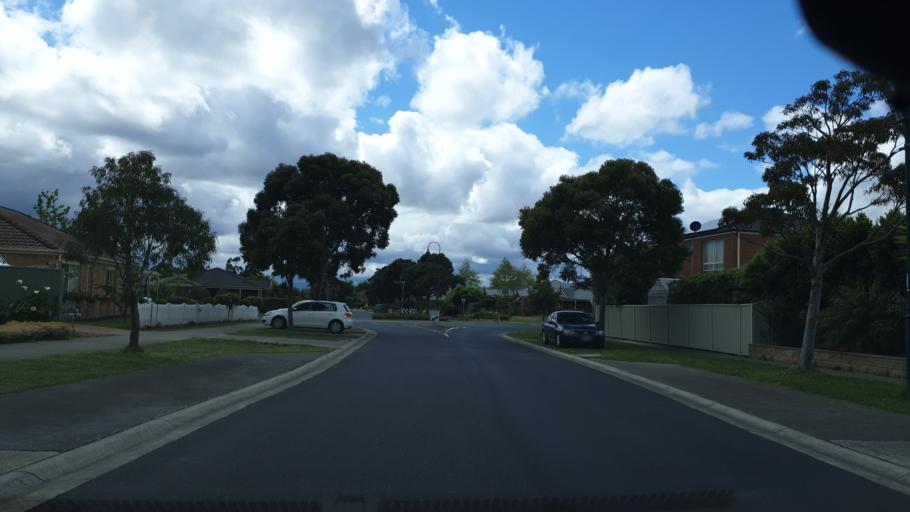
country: AU
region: Victoria
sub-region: Casey
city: Cranbourne East
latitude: -38.1052
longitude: 145.2961
